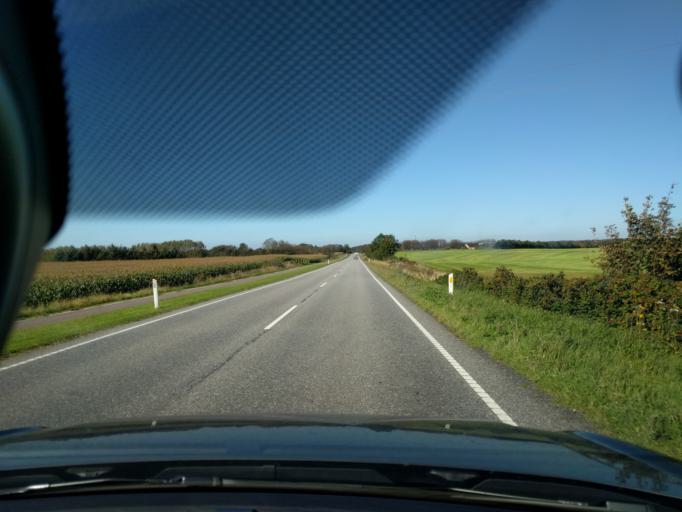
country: DK
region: North Denmark
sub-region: Mariagerfjord Kommune
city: Hobro
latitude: 56.6897
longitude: 9.6538
